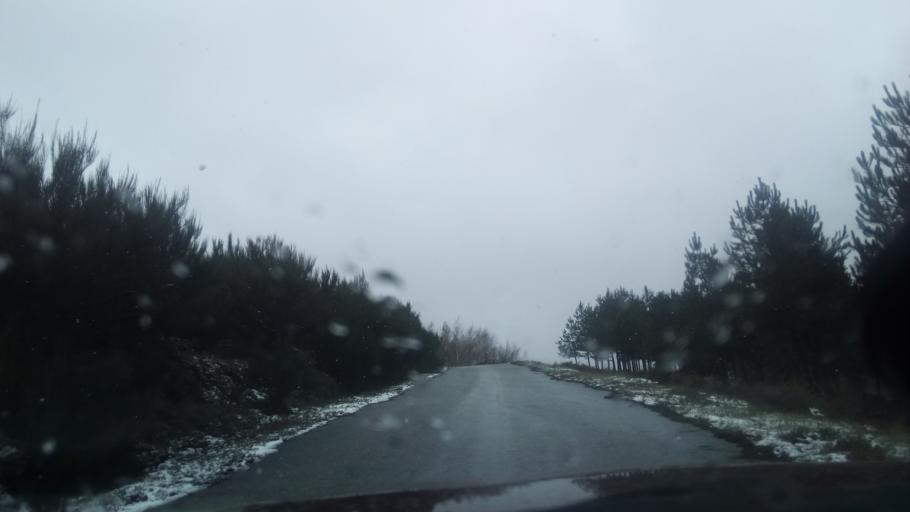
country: PT
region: Guarda
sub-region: Celorico da Beira
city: Celorico da Beira
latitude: 40.5176
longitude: -7.4542
